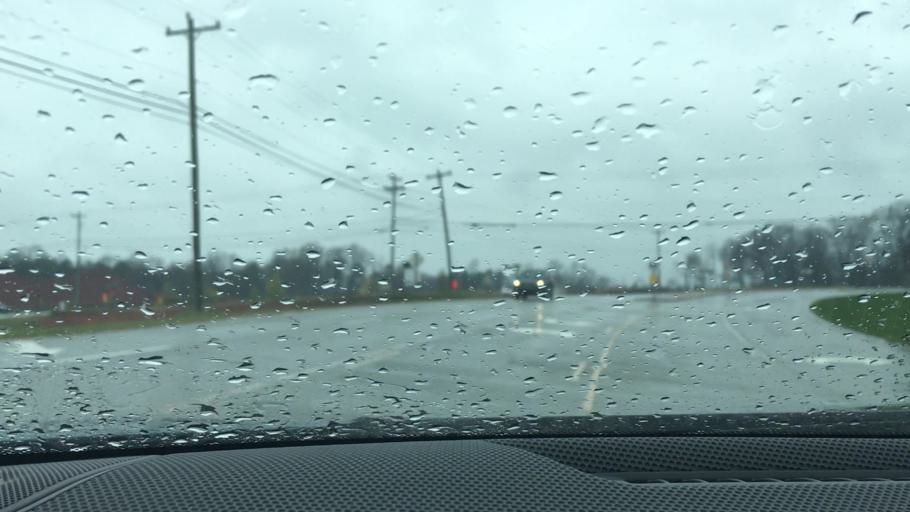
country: US
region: North Carolina
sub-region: Gaston County
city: Davidson
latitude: 35.5283
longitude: -80.8650
